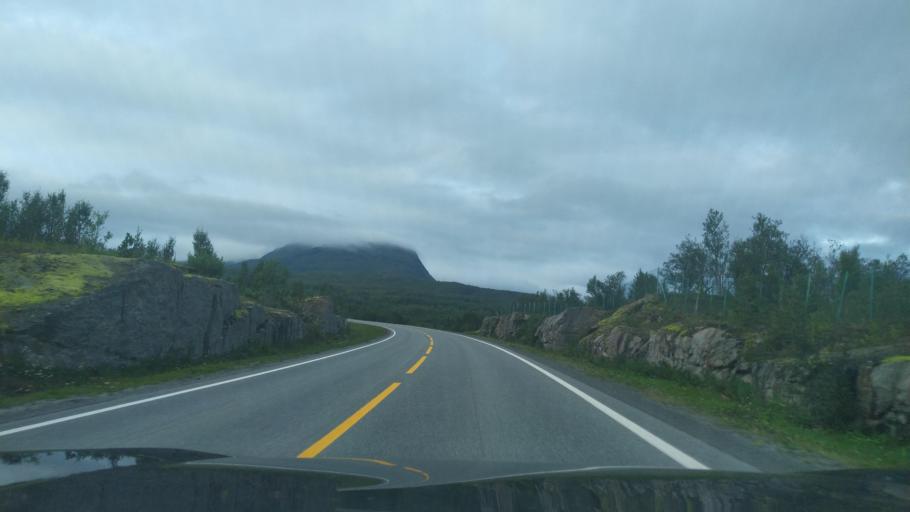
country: NO
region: Nordland
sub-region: Narvik
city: Narvik
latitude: 68.5235
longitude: 17.3953
